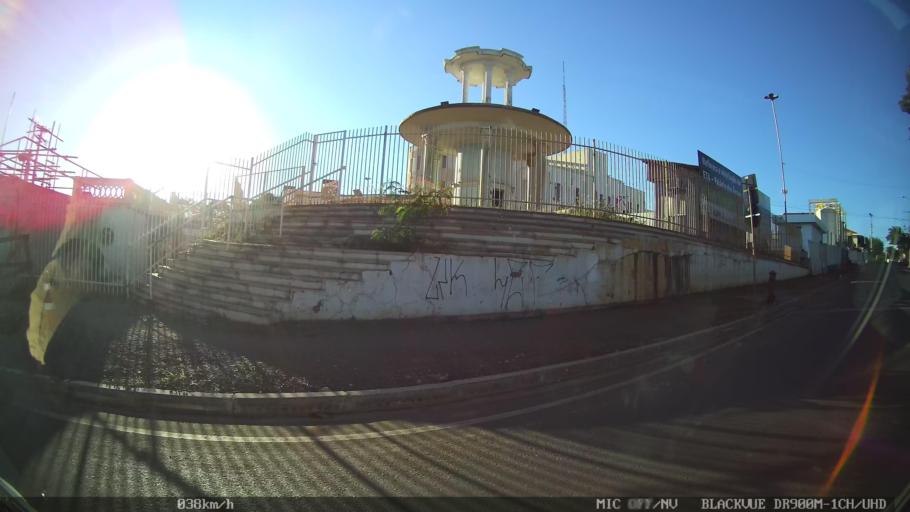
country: BR
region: Sao Paulo
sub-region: Sao Jose Do Rio Preto
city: Sao Jose do Rio Preto
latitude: -20.8084
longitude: -49.3734
